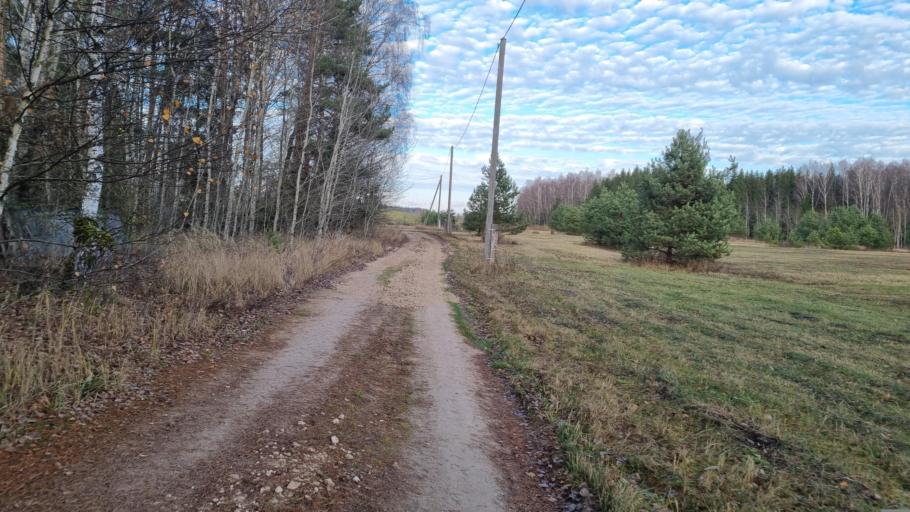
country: LV
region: Kekava
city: Kekava
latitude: 56.7835
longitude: 24.2475
